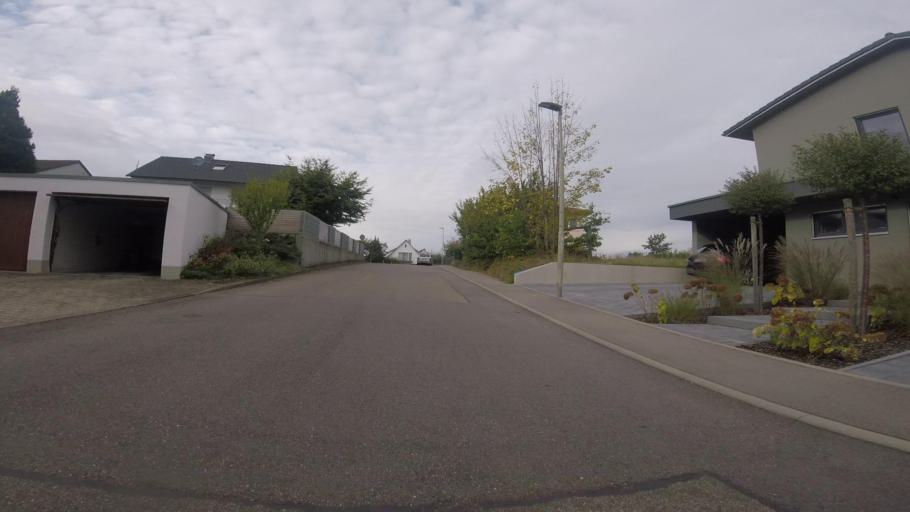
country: DE
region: Baden-Wuerttemberg
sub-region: Regierungsbezirk Stuttgart
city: Backnang
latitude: 48.9531
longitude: 9.4267
